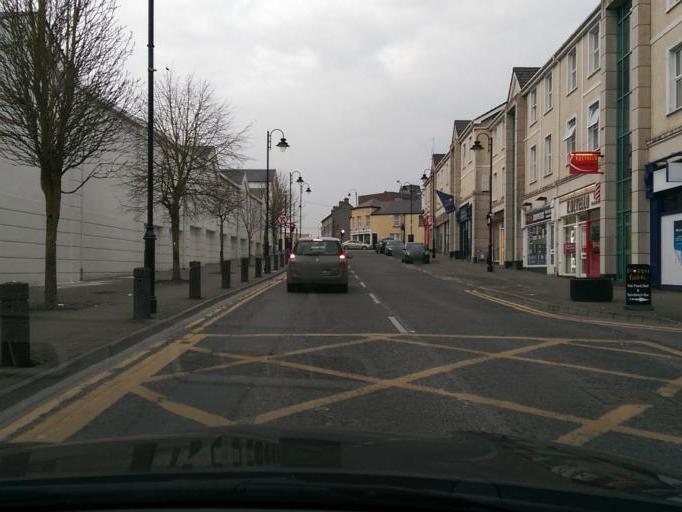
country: IE
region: Leinster
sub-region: An Iarmhi
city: Athlone
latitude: 53.4220
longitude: -7.9351
